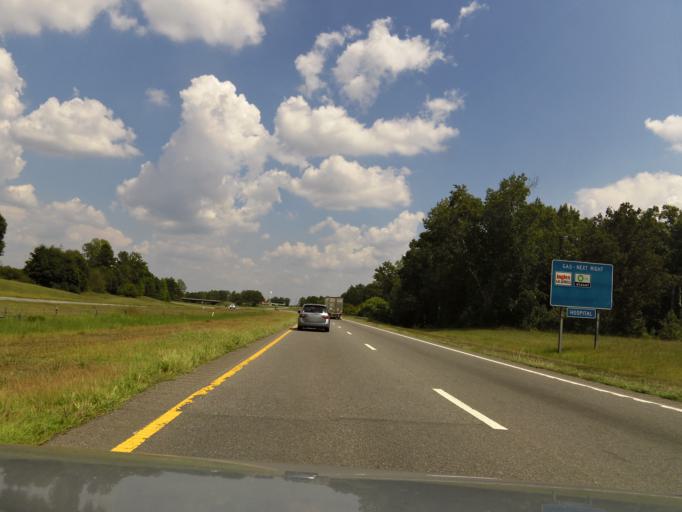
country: US
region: North Carolina
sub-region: Cleveland County
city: White Plains
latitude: 35.2461
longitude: -81.4149
